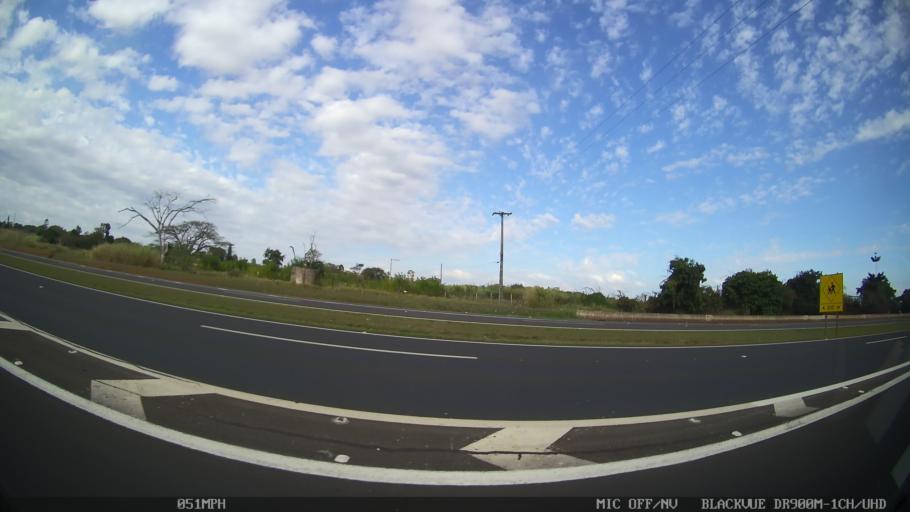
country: BR
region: Sao Paulo
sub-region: Iracemapolis
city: Iracemapolis
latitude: -22.5887
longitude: -47.4604
